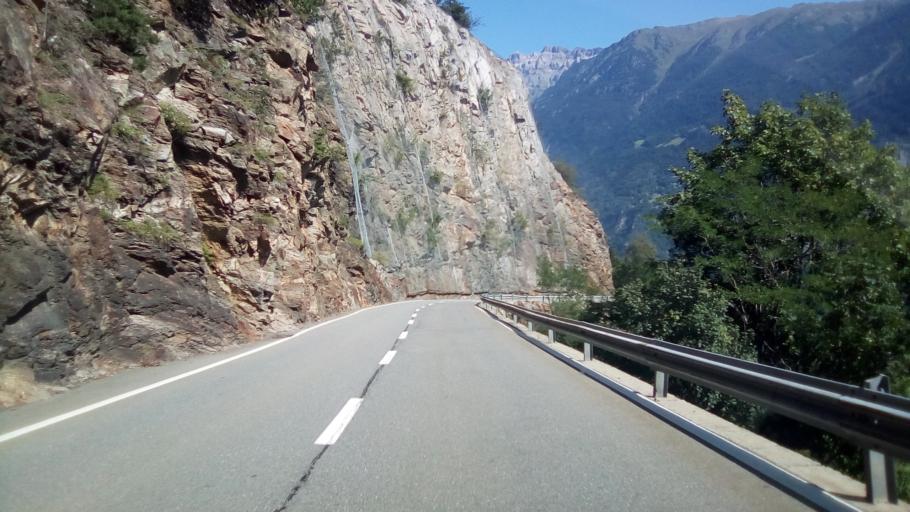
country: CH
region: Valais
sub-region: Saint-Maurice District
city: Vernayaz
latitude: 46.1254
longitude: 7.0337
